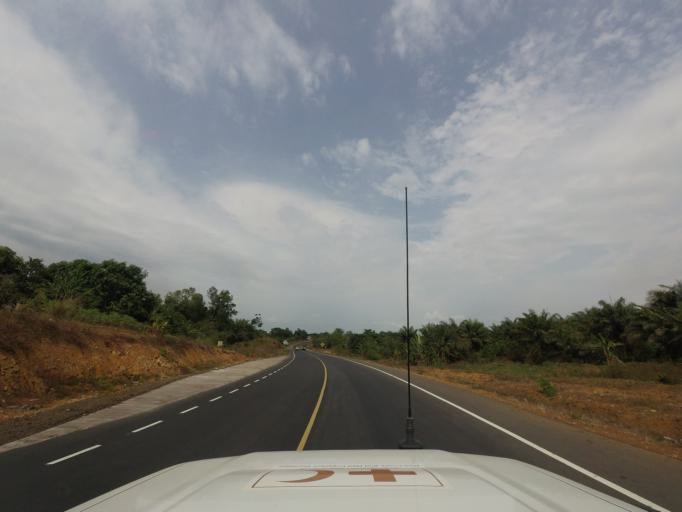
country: LR
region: Montserrado
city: Bensonville City
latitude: 6.3989
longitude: -10.5169
